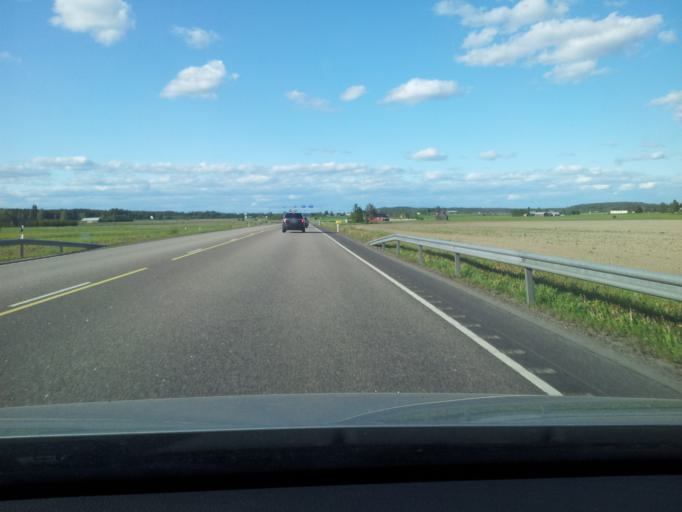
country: FI
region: Kymenlaakso
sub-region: Kouvola
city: Elimaeki
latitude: 60.7405
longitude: 26.4459
